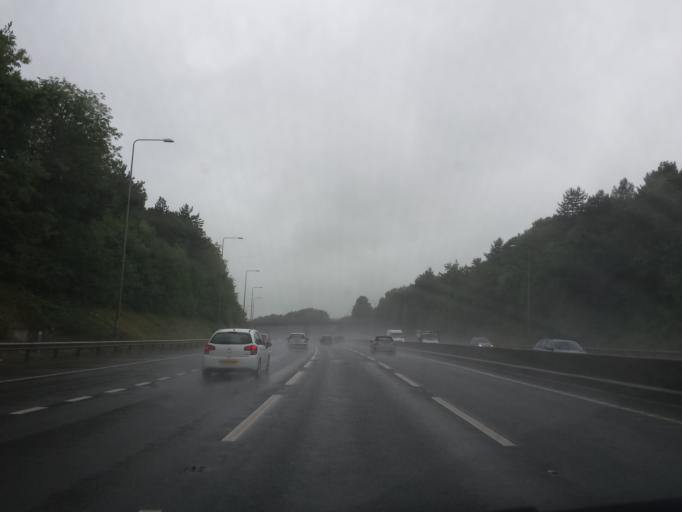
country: GB
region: England
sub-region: Derbyshire
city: Ilkeston
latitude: 52.9302
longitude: -1.2995
